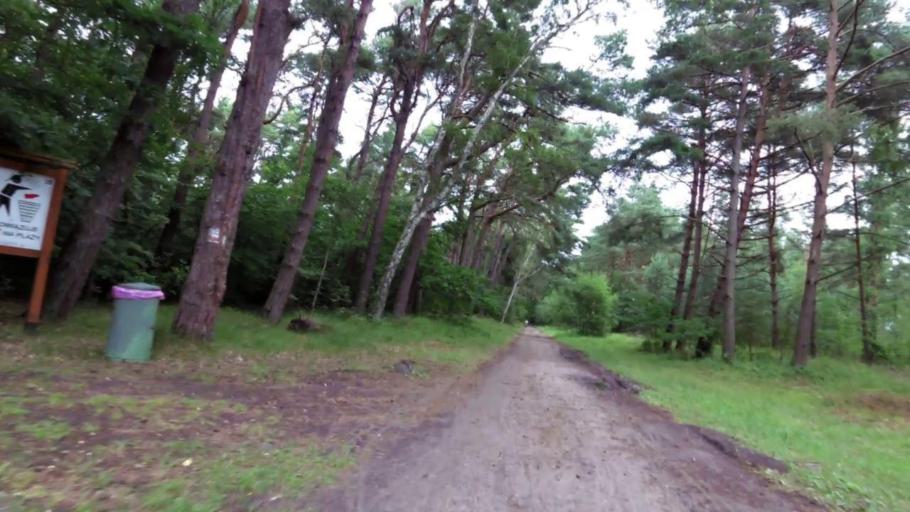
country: PL
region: West Pomeranian Voivodeship
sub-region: Powiat slawienski
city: Darlowo
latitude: 54.5053
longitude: 16.4630
